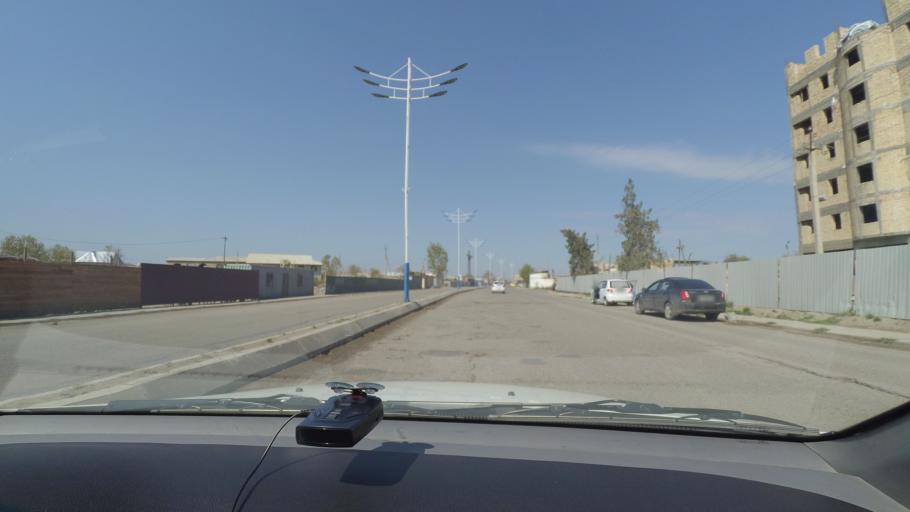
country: UZ
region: Bukhara
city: Bukhara
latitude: 39.7742
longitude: 64.4473
